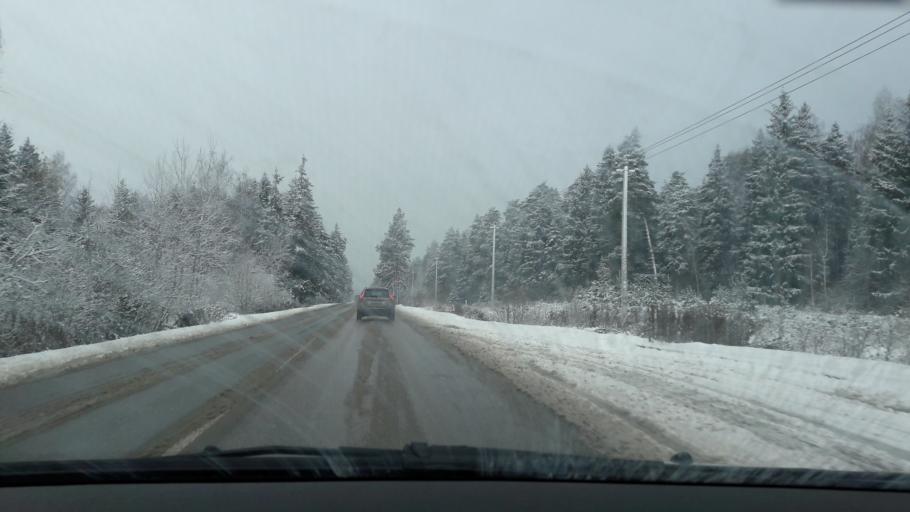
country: RU
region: Moskovskaya
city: Zvenigorod
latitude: 55.6383
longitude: 36.8479
